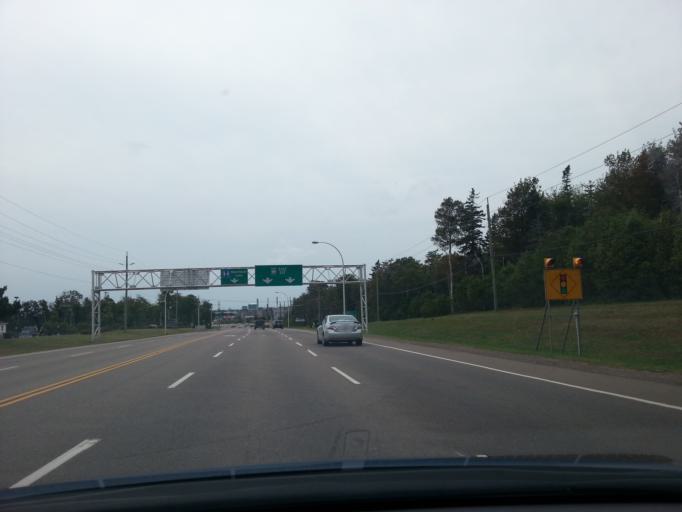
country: CA
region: Prince Edward Island
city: Charlottetown
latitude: 46.2564
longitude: -63.1017
